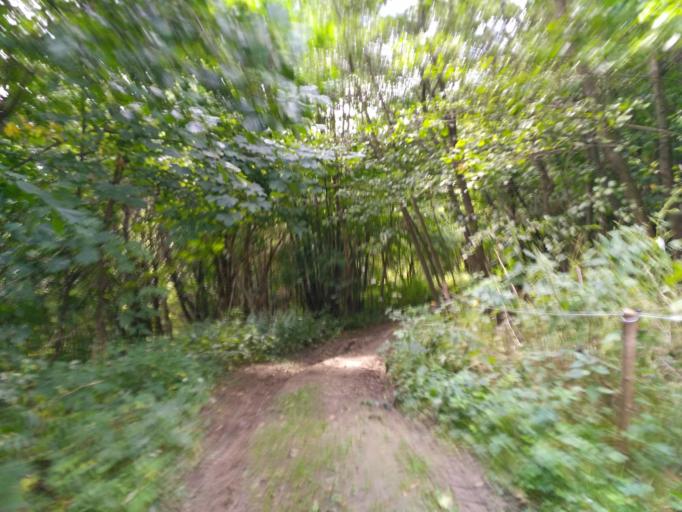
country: PL
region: Subcarpathian Voivodeship
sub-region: Powiat krosnienski
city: Iwonicz-Zdroj
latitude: 49.5728
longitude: 21.7766
